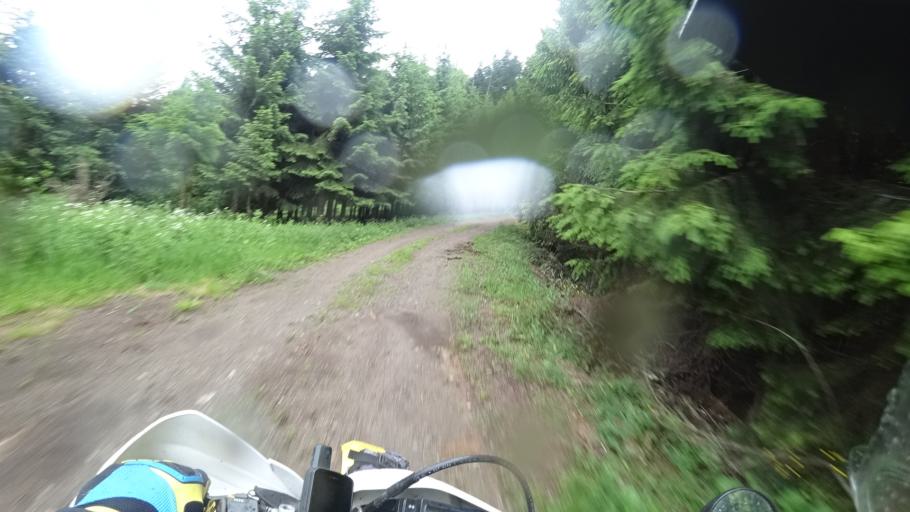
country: HR
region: Primorsko-Goranska
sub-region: Grad Delnice
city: Delnice
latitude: 45.3606
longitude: 14.8946
